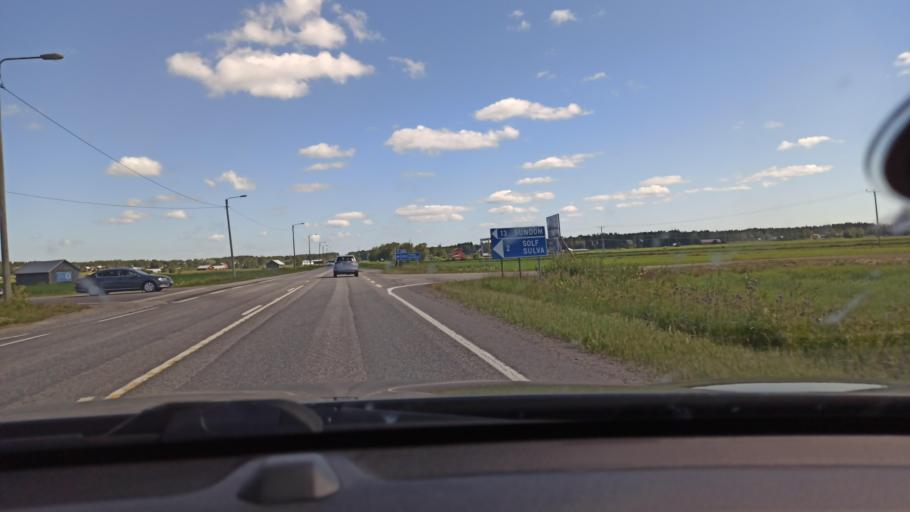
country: FI
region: Ostrobothnia
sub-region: Vaasa
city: Teeriniemi
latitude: 63.0036
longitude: 21.6789
